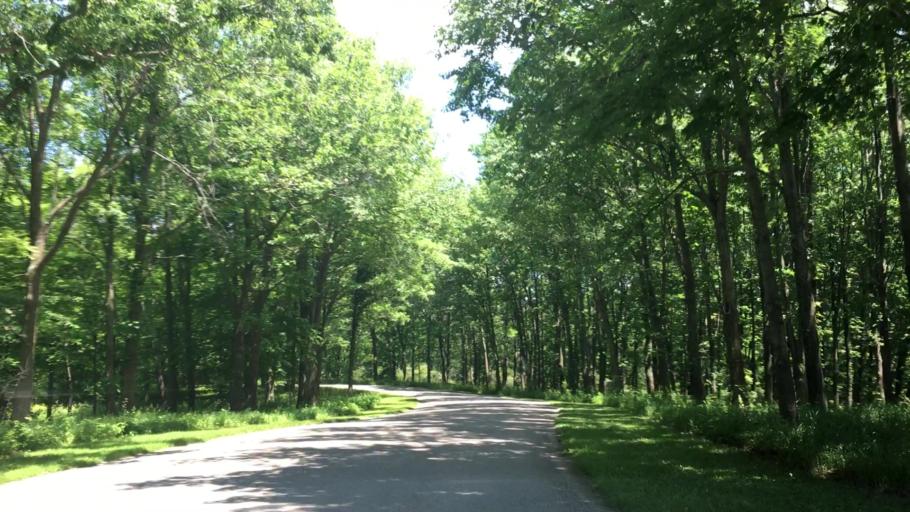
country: US
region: Iowa
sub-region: Johnson County
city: Tiffin
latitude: 41.7254
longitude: -91.7240
